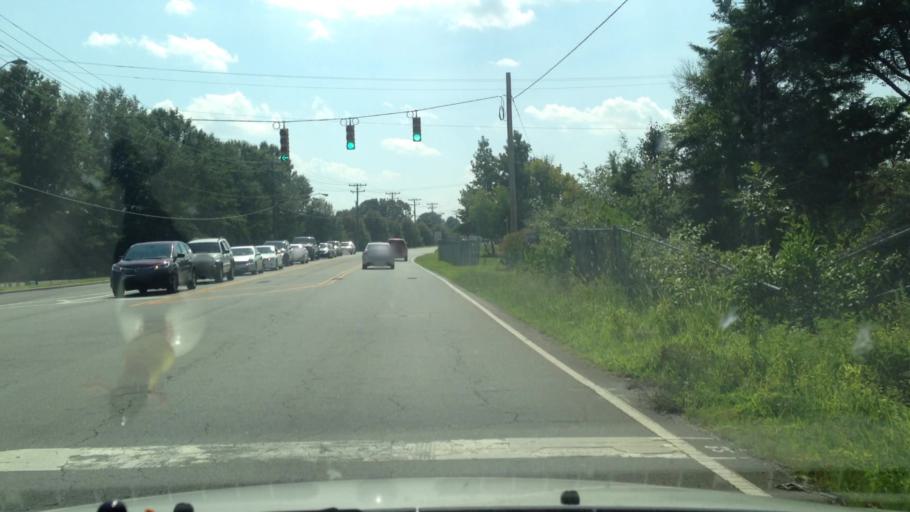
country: US
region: North Carolina
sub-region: Forsyth County
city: Kernersville
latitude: 36.1289
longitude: -80.0611
